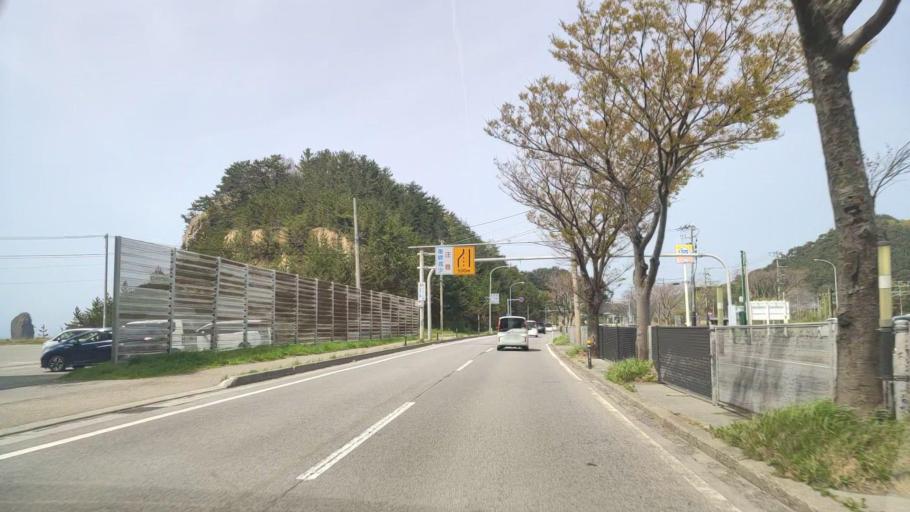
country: JP
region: Aomori
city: Aomori Shi
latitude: 40.8970
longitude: 140.8602
